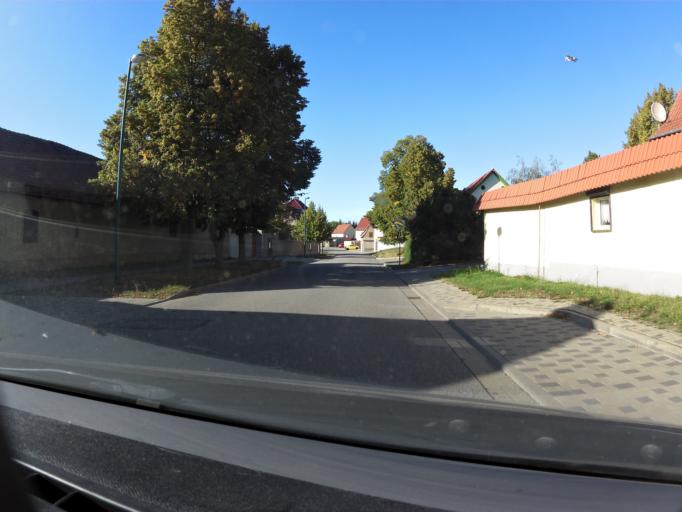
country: DE
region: Saxony-Anhalt
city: Hedersleben
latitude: 51.8613
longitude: 11.2512
